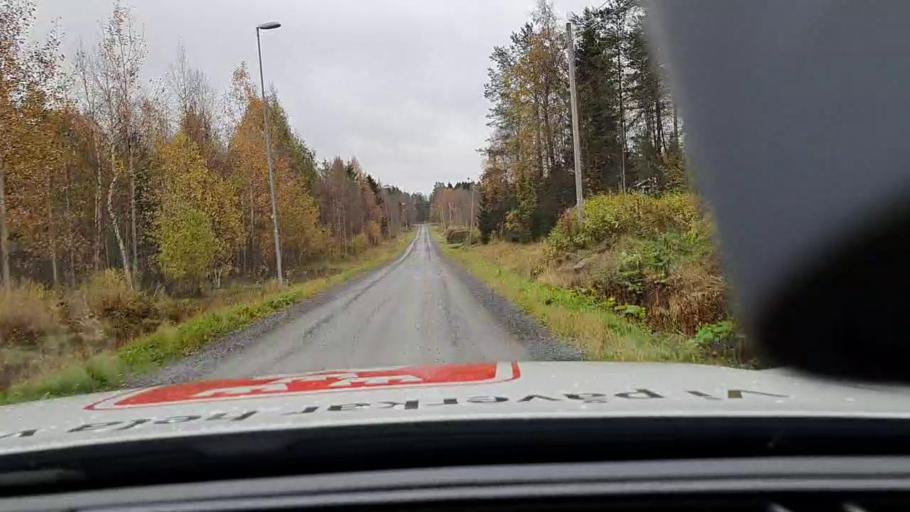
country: FI
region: Lapland
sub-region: Kemi-Tornio
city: Tornio
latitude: 65.9768
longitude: 24.0204
